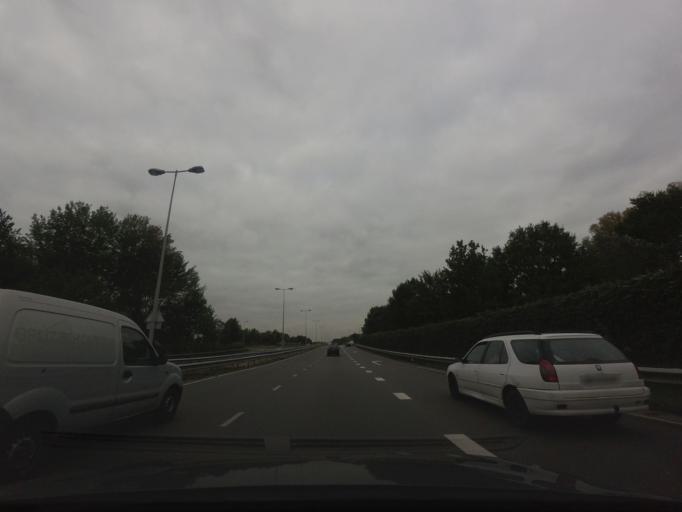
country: NL
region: North Holland
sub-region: Gemeente Ouder-Amstel
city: Duivendrecht
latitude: 52.3296
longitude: 4.9520
